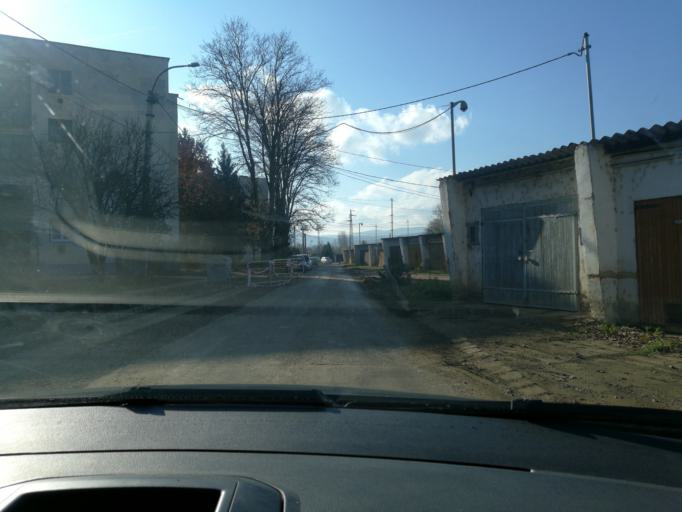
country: HU
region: Nograd
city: Batonyterenye
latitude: 47.9877
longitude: 19.8233
